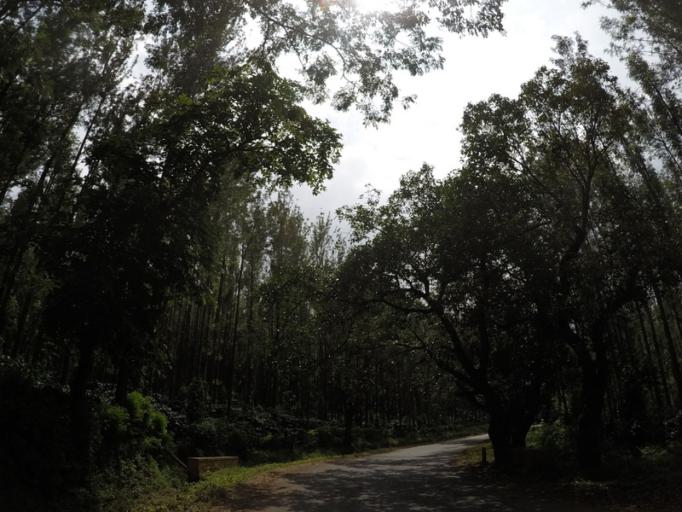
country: IN
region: Karnataka
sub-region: Chikmagalur
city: Chikmagalur
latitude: 13.3852
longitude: 75.7594
